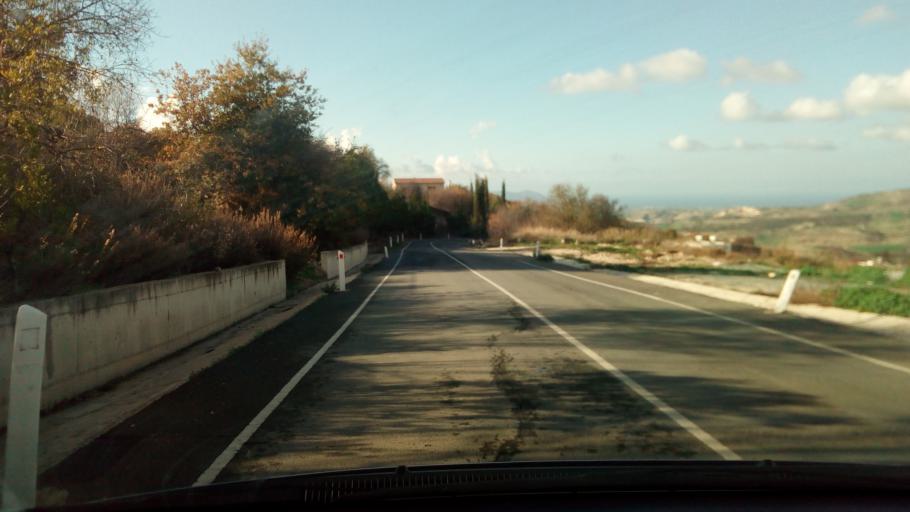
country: CY
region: Pafos
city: Polis
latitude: 34.9395
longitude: 32.5093
